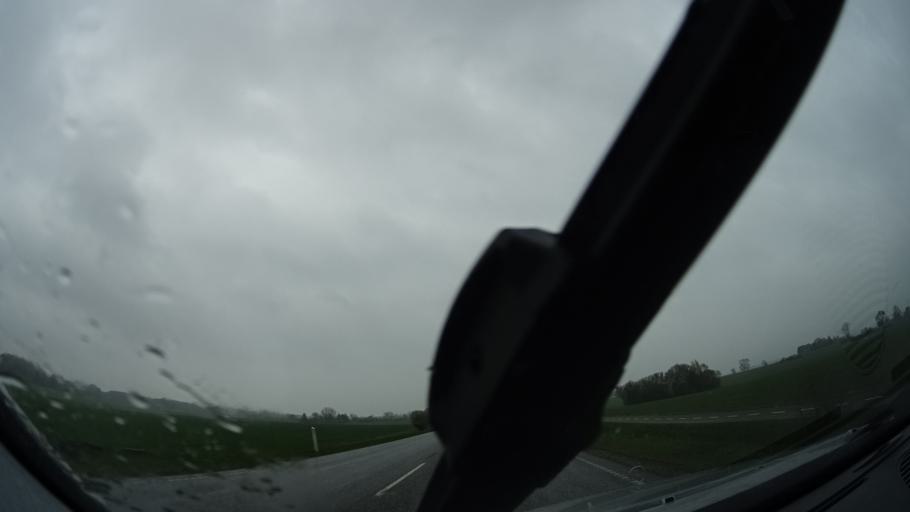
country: DK
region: Zealand
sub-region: Holbaek Kommune
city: Holbaek
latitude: 55.7399
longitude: 11.6234
